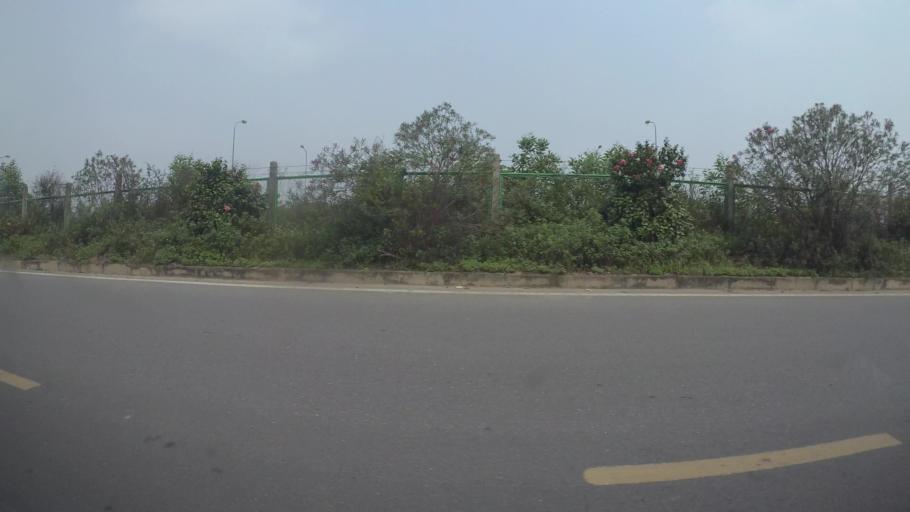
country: VN
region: Ha Noi
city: Quoc Oai
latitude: 20.9960
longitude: 105.5926
